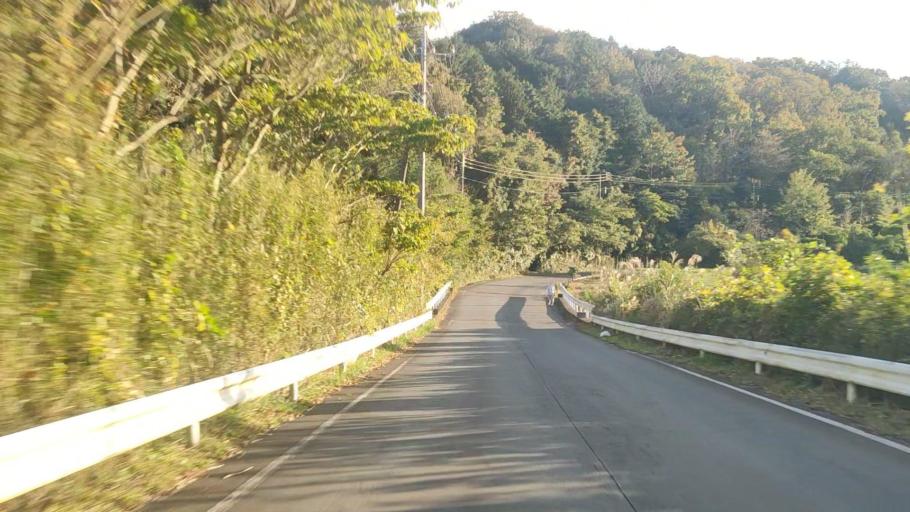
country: JP
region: Shizuoka
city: Mishima
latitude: 35.1514
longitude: 138.9399
